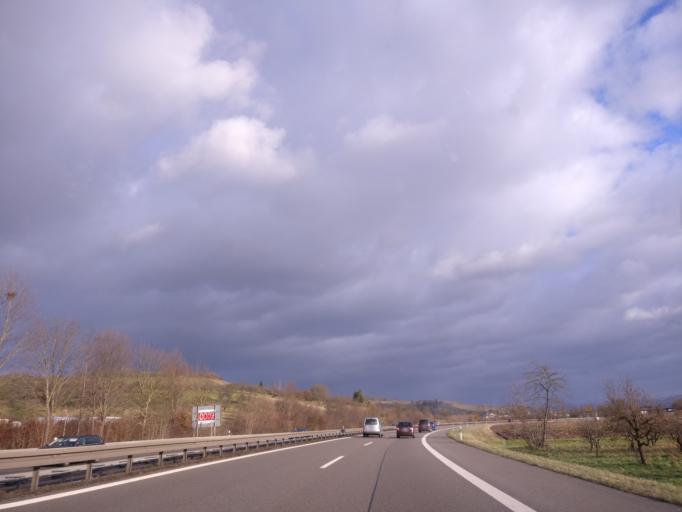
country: DE
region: Baden-Wuerttemberg
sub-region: Regierungsbezirk Stuttgart
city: Weinstadt-Endersbach
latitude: 48.8175
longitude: 9.3972
